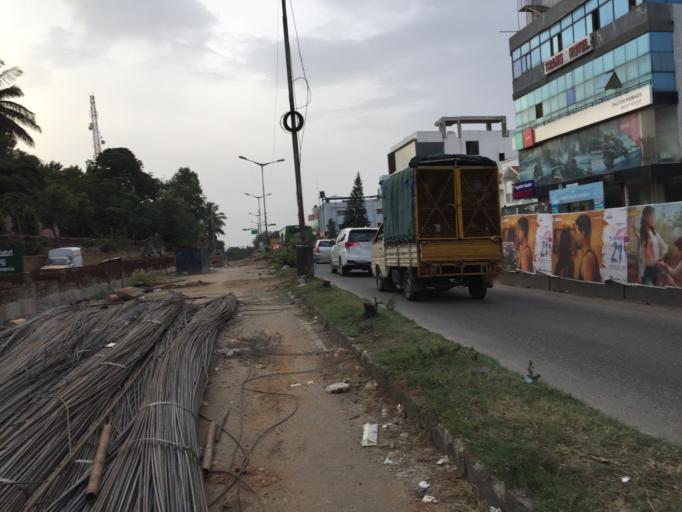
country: IN
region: Karnataka
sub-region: Bangalore Urban
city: Bangalore
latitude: 12.9295
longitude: 77.5445
